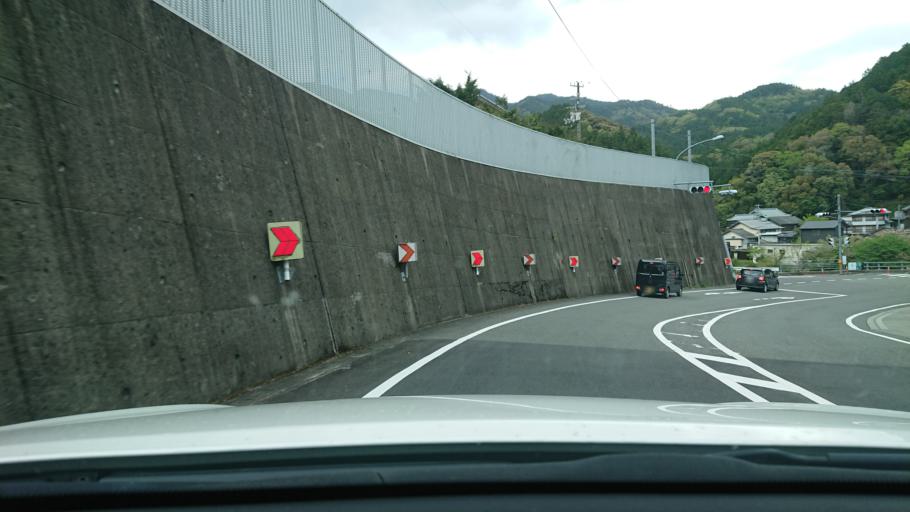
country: JP
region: Tokushima
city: Ishii
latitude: 33.9206
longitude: 134.4260
